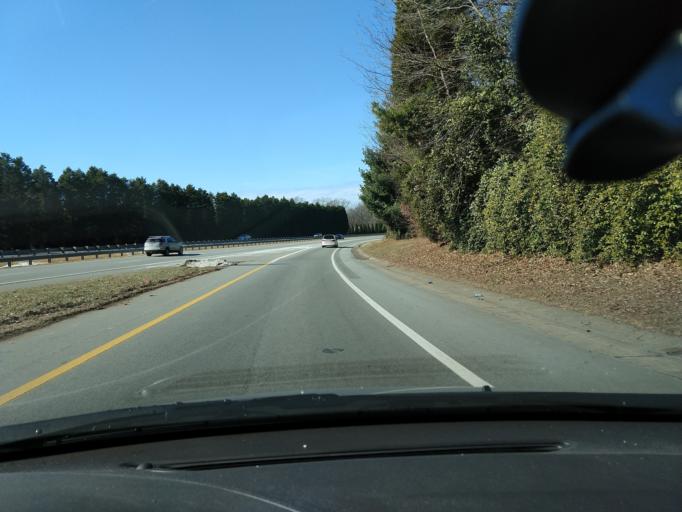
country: US
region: North Carolina
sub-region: Guilford County
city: Greensboro
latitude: 36.1141
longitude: -79.8527
